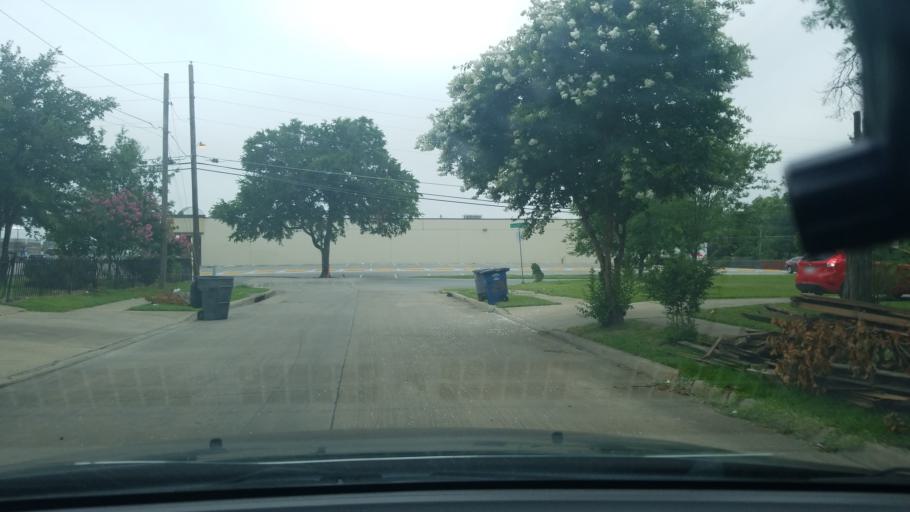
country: US
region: Texas
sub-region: Dallas County
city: Balch Springs
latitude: 32.7528
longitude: -96.6844
